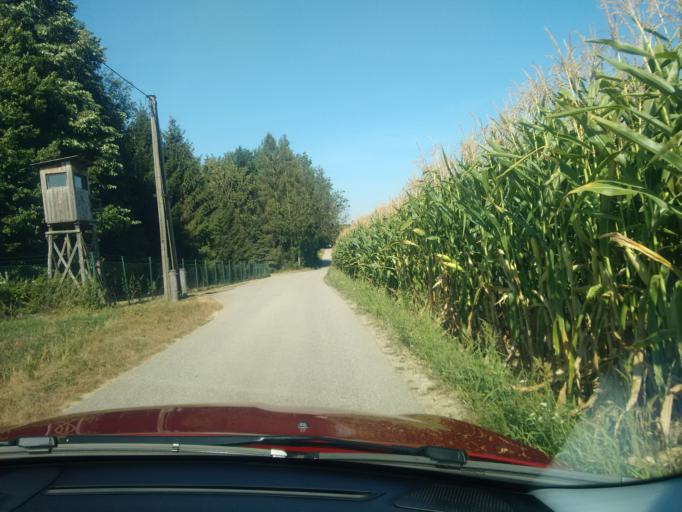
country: AT
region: Upper Austria
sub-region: Wels-Land
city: Sattledt
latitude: 48.0898
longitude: 14.0738
